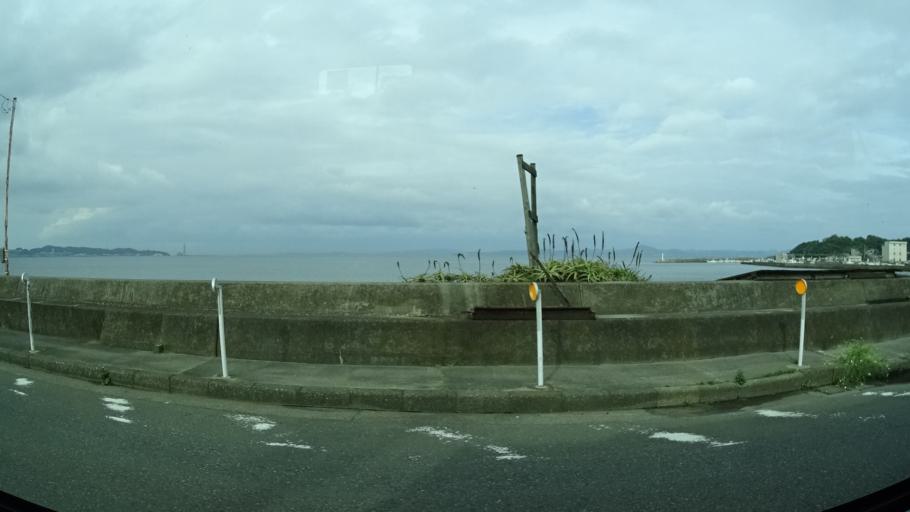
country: JP
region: Kanagawa
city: Miura
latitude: 35.1608
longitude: 139.6616
